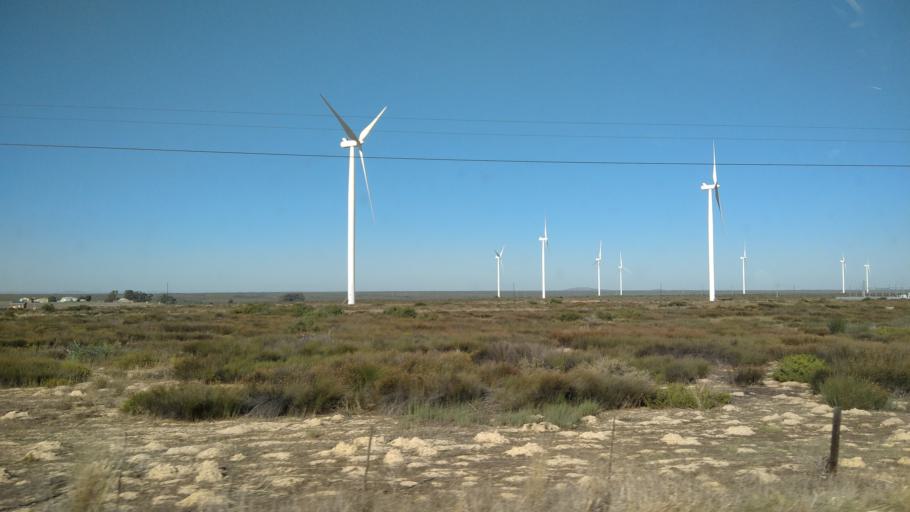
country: ZA
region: Western Cape
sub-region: West Coast District Municipality
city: Moorreesburg
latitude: -33.0912
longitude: 18.4075
